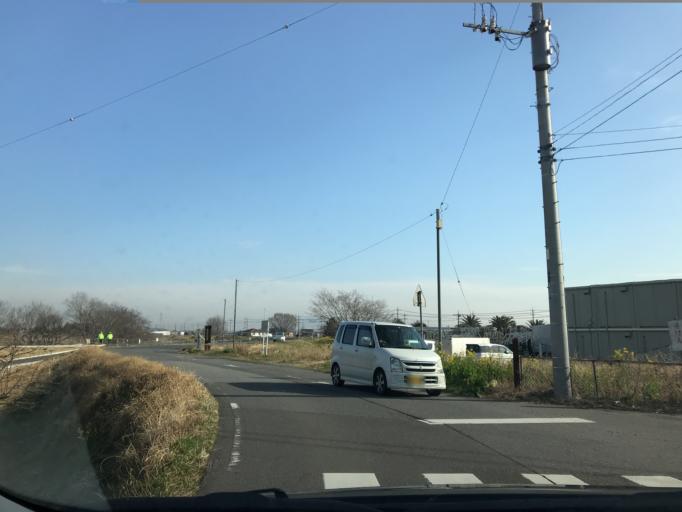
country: JP
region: Ibaraki
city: Mitsukaido
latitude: 35.9908
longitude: 139.9786
